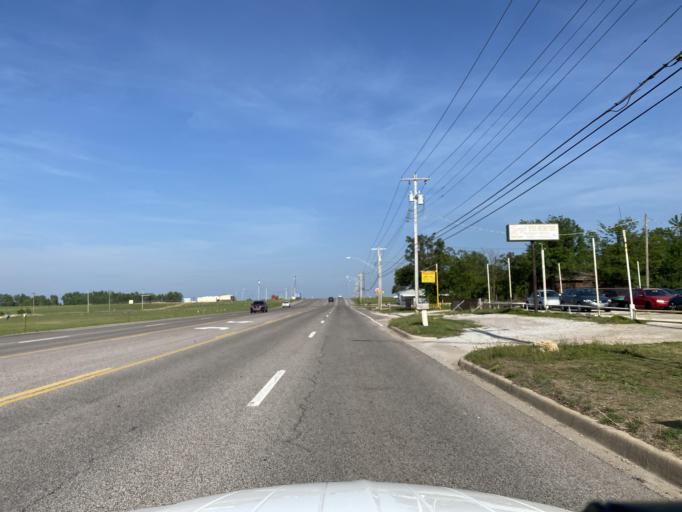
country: US
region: Oklahoma
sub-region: Oklahoma County
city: Nicoma Park
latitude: 35.4930
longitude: -97.3473
